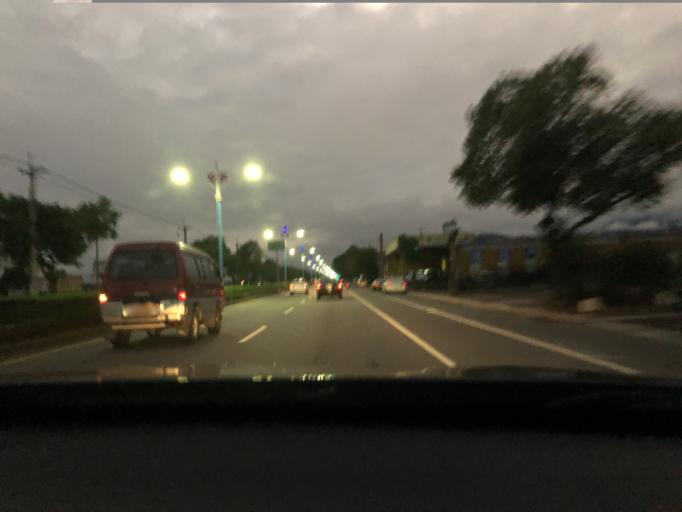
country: TW
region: Taiwan
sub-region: Hualien
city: Hualian
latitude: 23.9628
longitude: 121.5657
